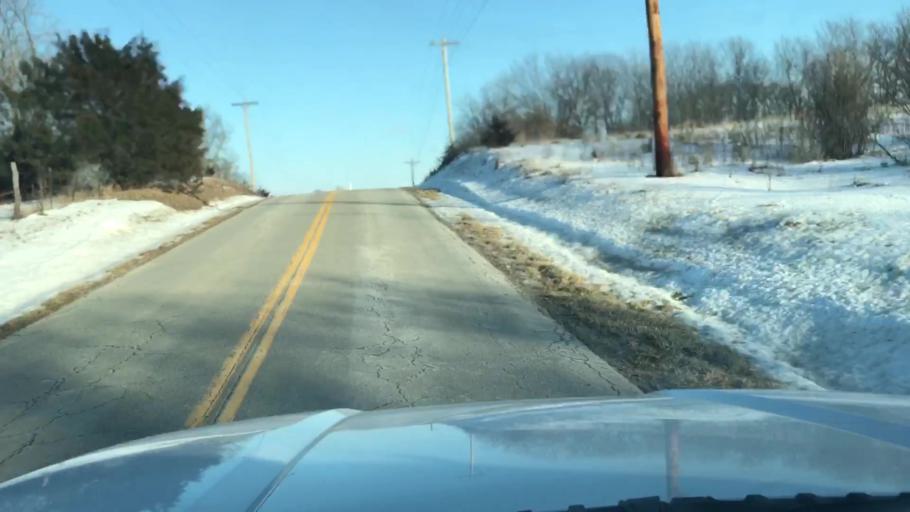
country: US
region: Missouri
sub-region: Andrew County
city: Savannah
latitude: 40.0247
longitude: -94.8945
